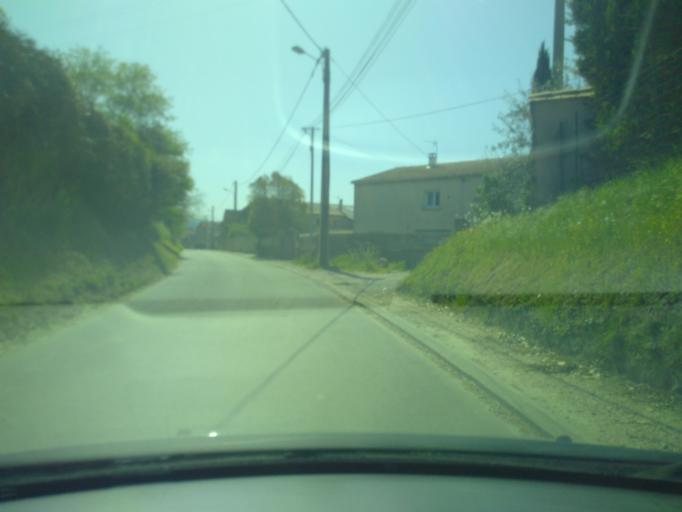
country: FR
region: Provence-Alpes-Cote d'Azur
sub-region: Departement du Vaucluse
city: Mazan
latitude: 44.0598
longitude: 5.1219
